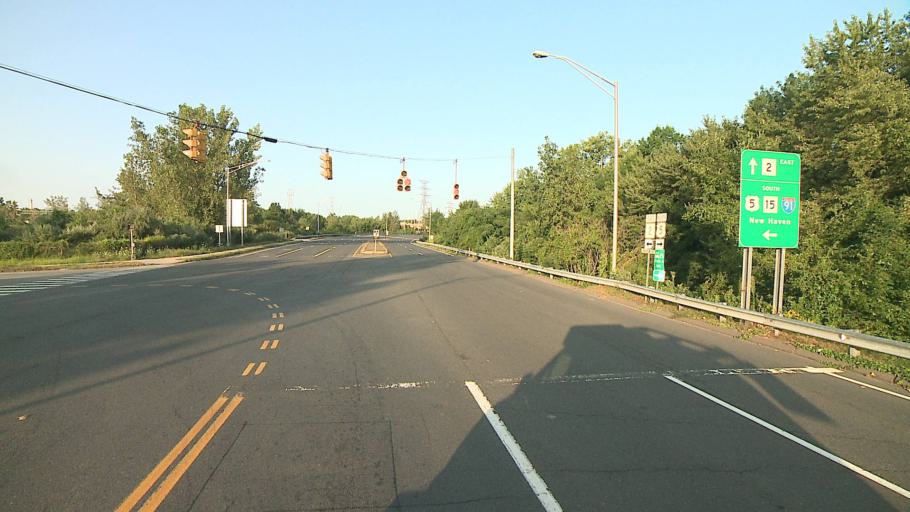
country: US
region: Connecticut
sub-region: Hartford County
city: Hartford
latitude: 41.7594
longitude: -72.6474
